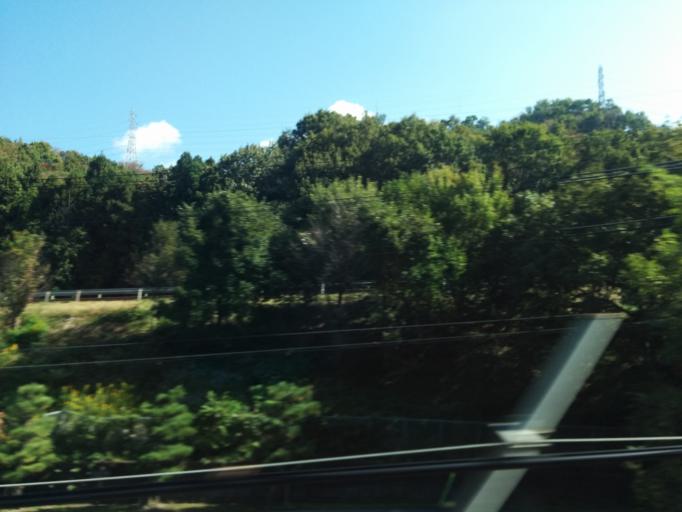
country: JP
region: Shiga Prefecture
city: Hikone
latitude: 35.2661
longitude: 136.2789
